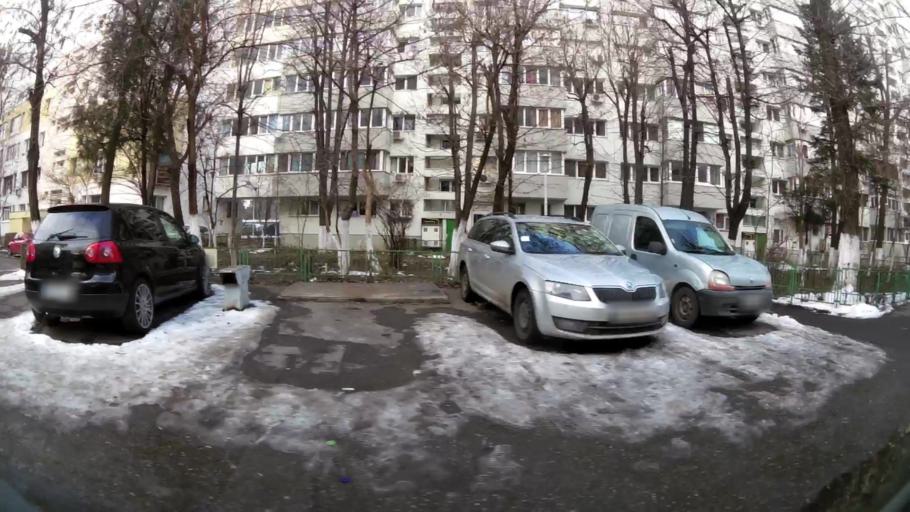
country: RO
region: Bucuresti
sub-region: Municipiul Bucuresti
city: Bucharest
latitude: 44.4209
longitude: 26.1428
